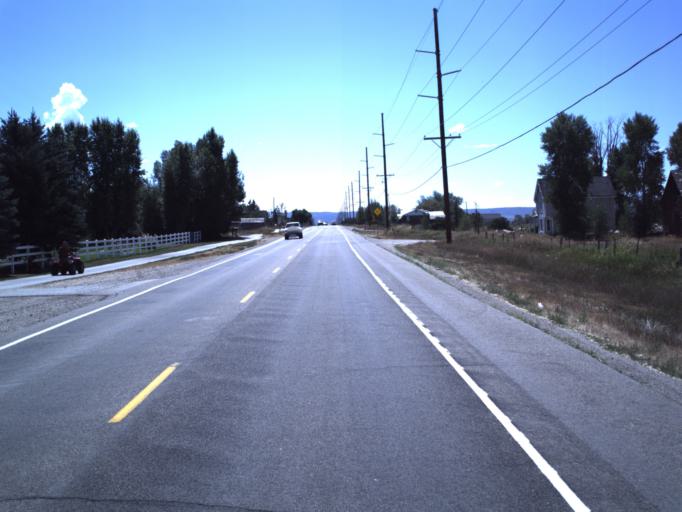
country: US
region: Utah
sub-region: Summit County
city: Oakley
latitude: 40.6963
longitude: -111.2811
